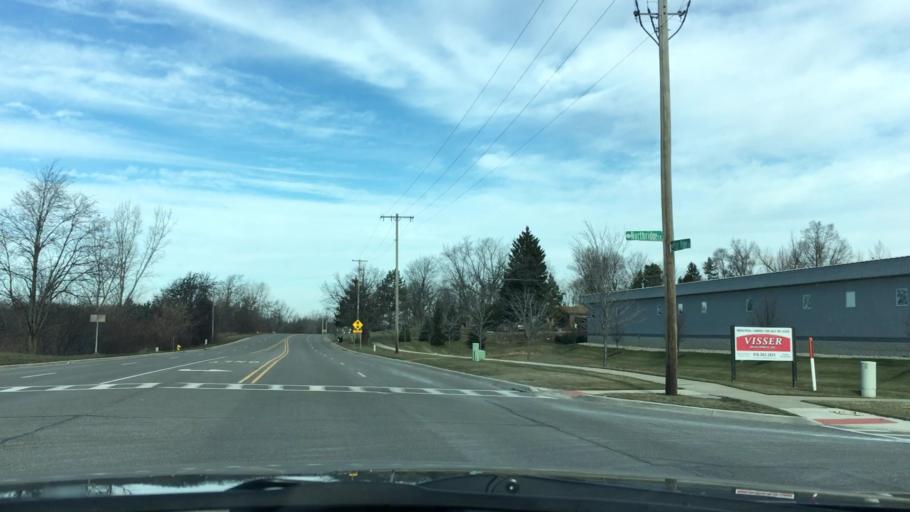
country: US
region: Michigan
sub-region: Kent County
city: Walker
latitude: 43.0264
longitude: -85.7636
